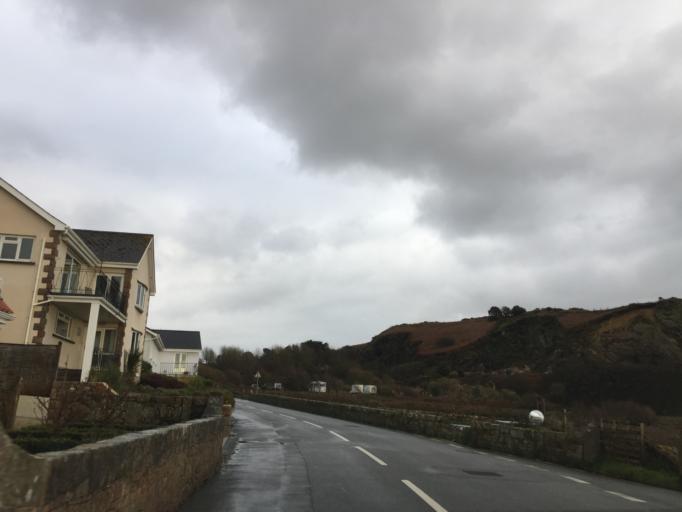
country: JE
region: St Helier
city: Saint Helier
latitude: 49.2357
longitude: -2.2313
